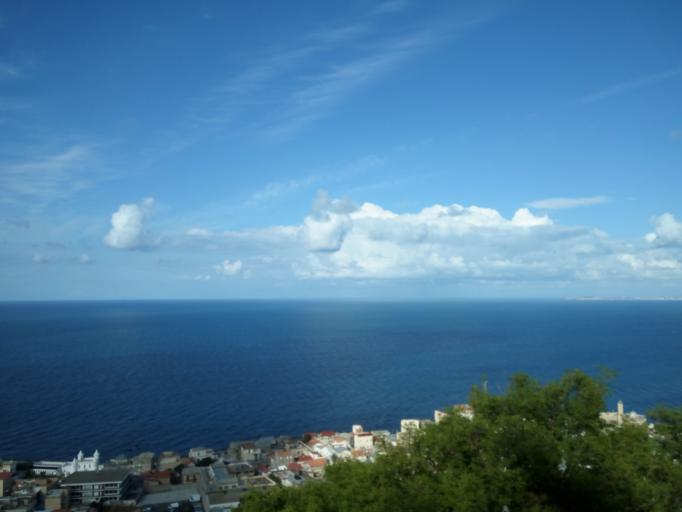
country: DZ
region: Alger
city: Algiers
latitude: 36.8010
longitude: 3.0432
